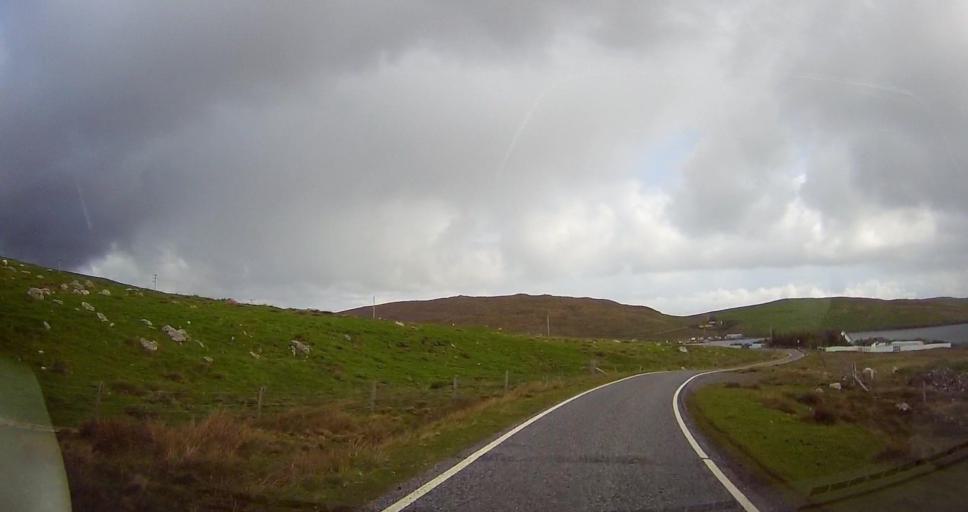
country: GB
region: Scotland
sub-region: Shetland Islands
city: Lerwick
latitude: 60.5342
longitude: -1.3605
